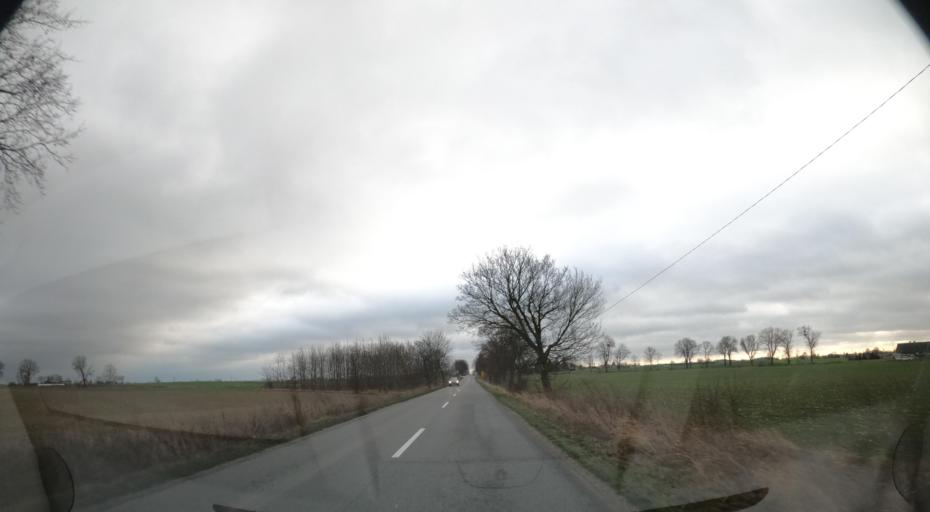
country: PL
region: Kujawsko-Pomorskie
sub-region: Powiat nakielski
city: Sadki
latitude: 53.1677
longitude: 17.4374
